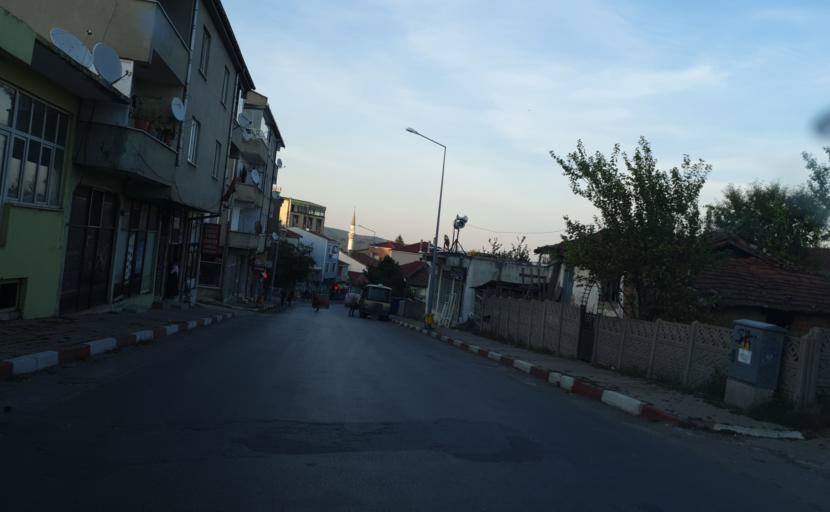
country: TR
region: Kirklareli
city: Sergen
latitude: 41.8235
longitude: 27.7638
